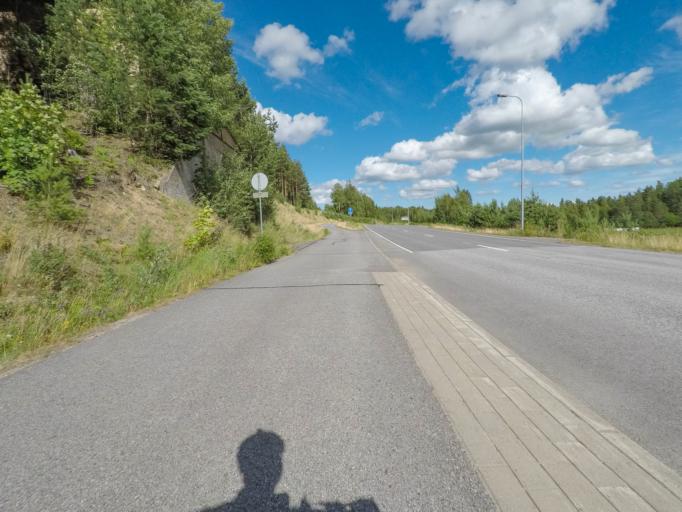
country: FI
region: South Karelia
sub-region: Lappeenranta
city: Lappeenranta
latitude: 61.0861
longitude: 28.3388
